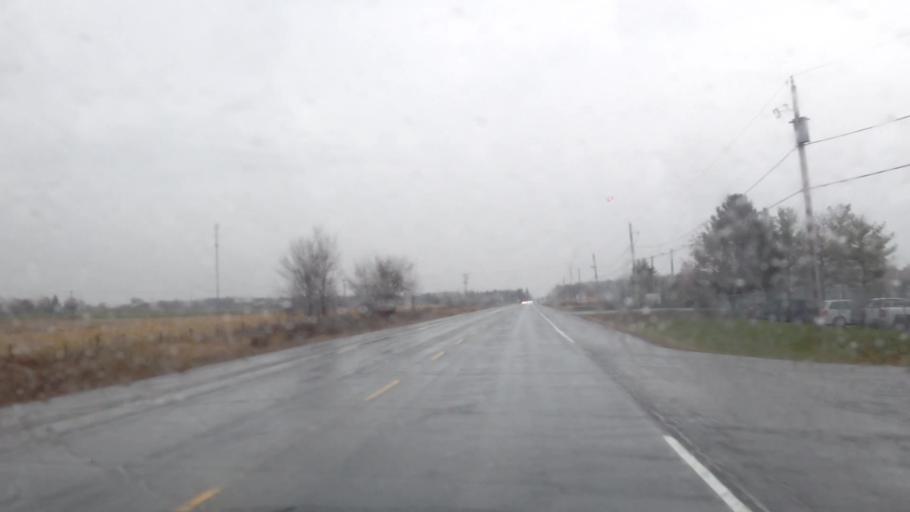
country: CA
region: Ontario
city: Clarence-Rockland
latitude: 45.4283
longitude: -75.4116
